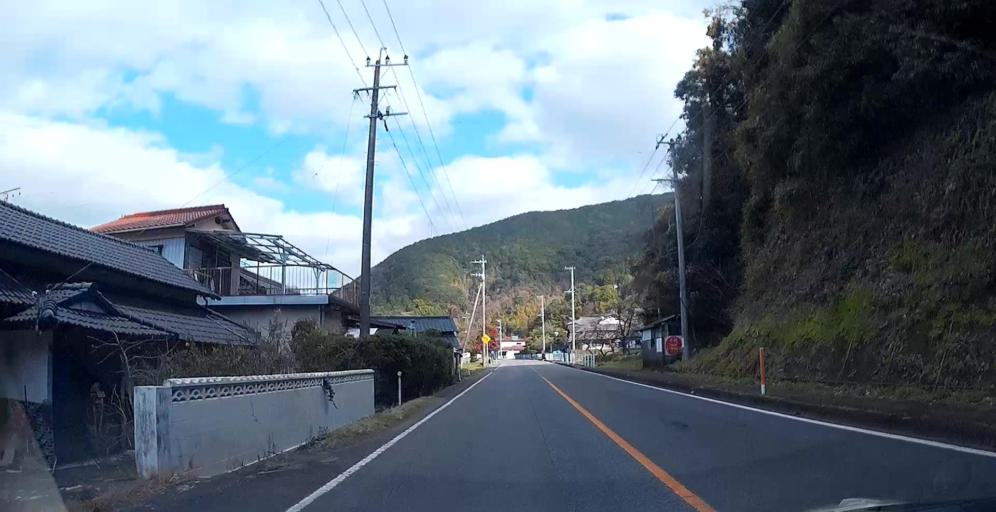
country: JP
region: Kumamoto
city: Yatsushiro
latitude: 32.4218
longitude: 130.5535
